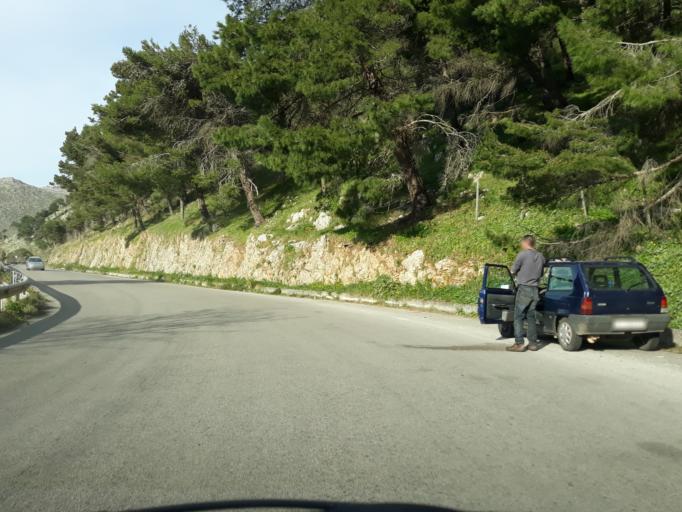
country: IT
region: Sicily
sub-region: Palermo
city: Torretta
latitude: 38.1210
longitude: 13.2456
